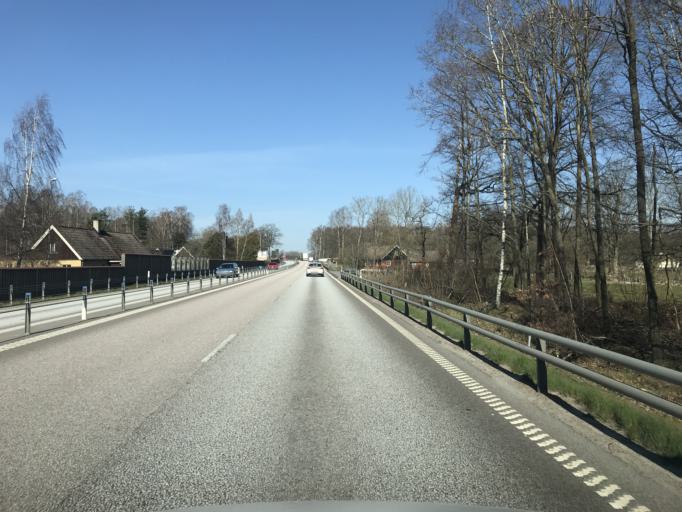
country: SE
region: Skane
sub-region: Hassleholms Kommun
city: Vinslov
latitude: 56.0763
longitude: 13.9291
